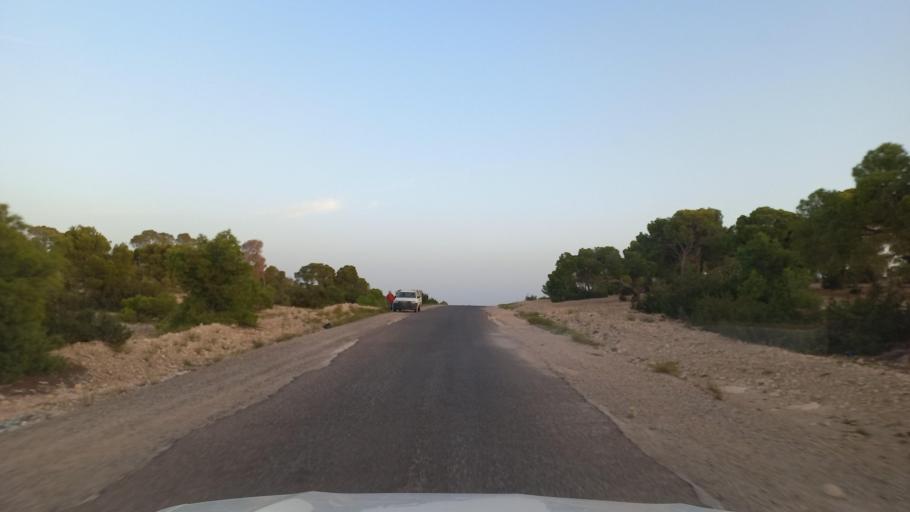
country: TN
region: Al Qasrayn
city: Sbiba
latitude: 35.4256
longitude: 8.9209
